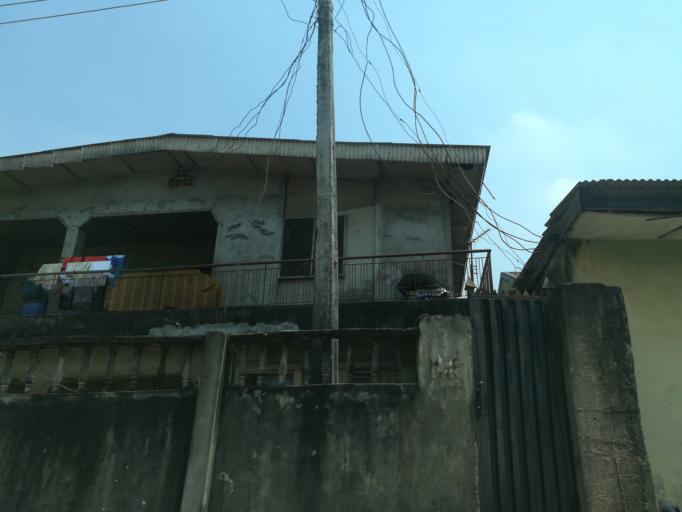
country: NG
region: Lagos
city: Ikorodu
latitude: 6.6219
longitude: 3.4922
